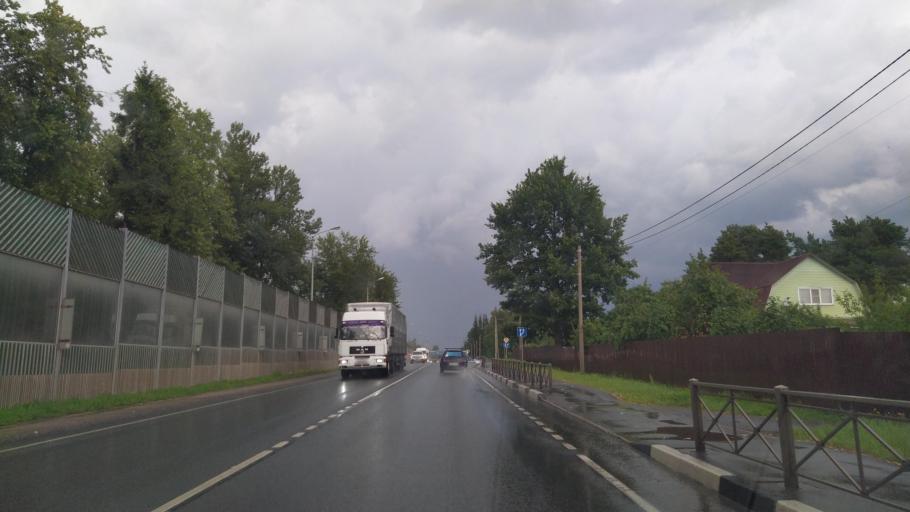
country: RU
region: Pskov
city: Pskov
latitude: 57.7570
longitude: 28.3825
